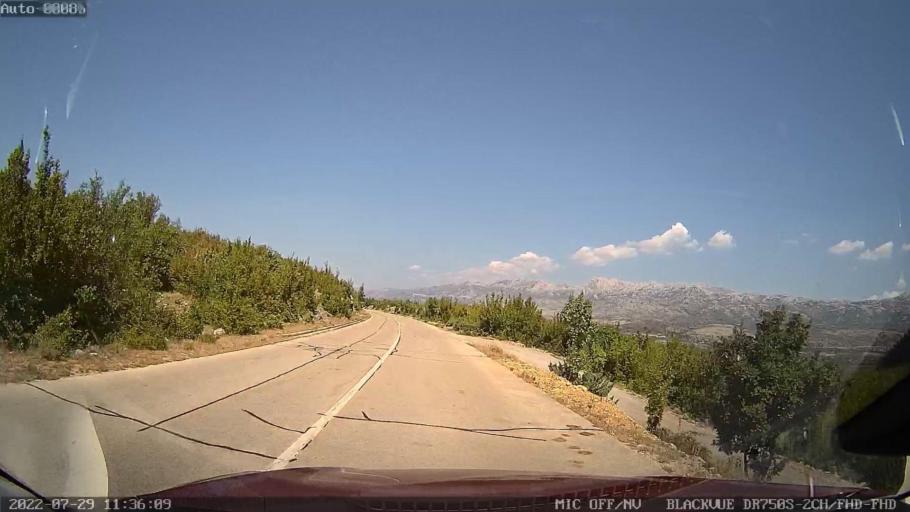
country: HR
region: Zadarska
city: Obrovac
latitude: 44.1876
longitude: 15.7025
